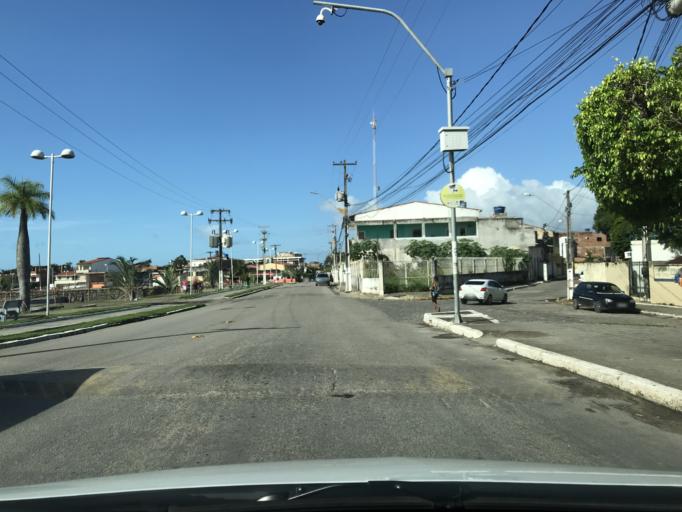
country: BR
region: Pernambuco
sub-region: Ipojuca
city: Ipojuca
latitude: -8.4378
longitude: -35.0125
